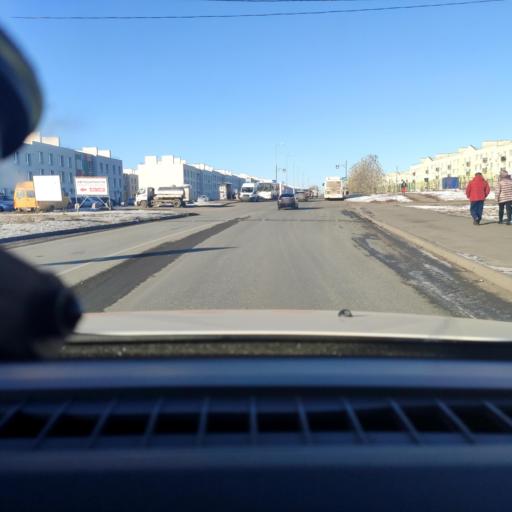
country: RU
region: Samara
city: Petra-Dubrava
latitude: 53.3087
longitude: 50.3097
